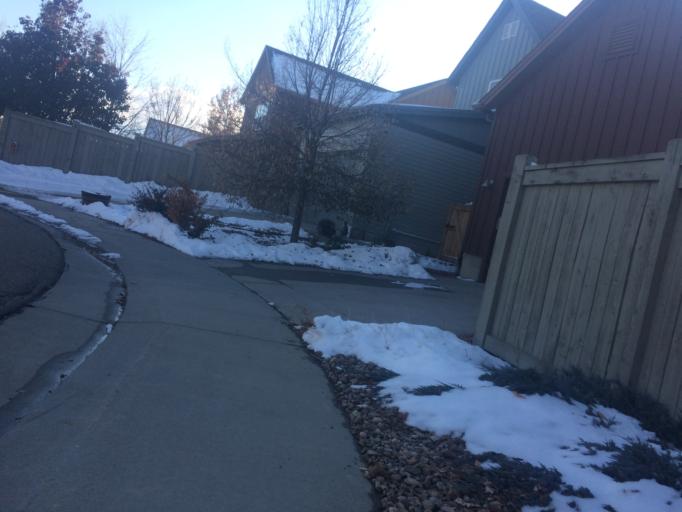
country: US
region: Colorado
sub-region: Boulder County
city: Louisville
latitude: 39.9939
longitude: -105.1233
